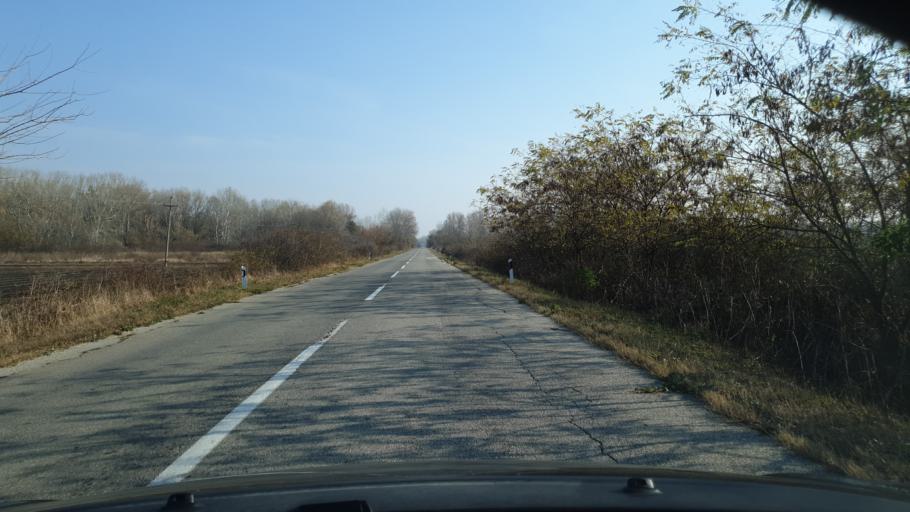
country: BG
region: Vidin
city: Bregovo
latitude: 44.1576
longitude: 22.6103
